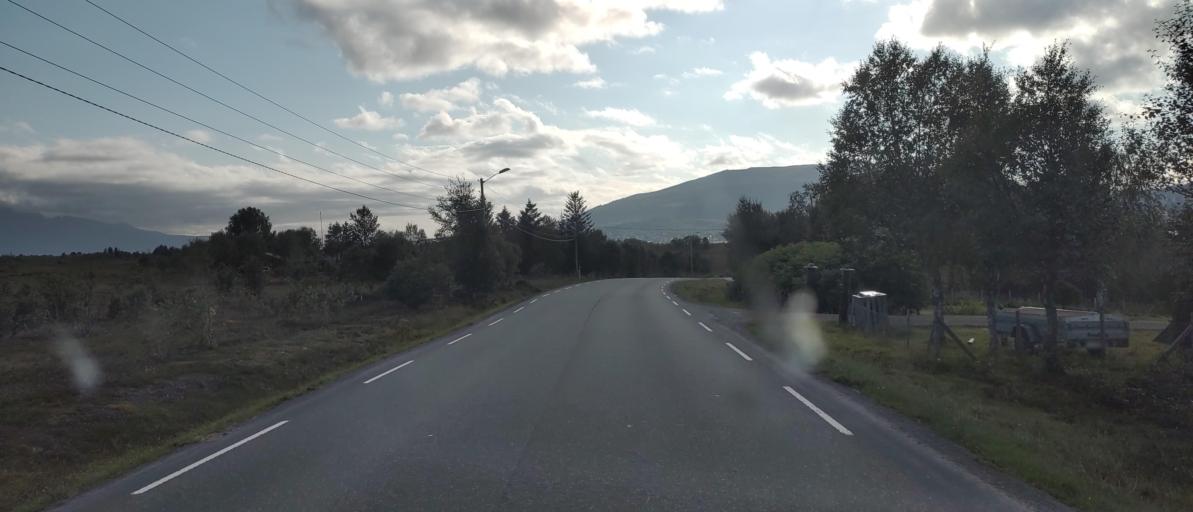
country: NO
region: Nordland
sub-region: Sortland
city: Sortland
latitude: 68.7186
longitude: 15.4551
